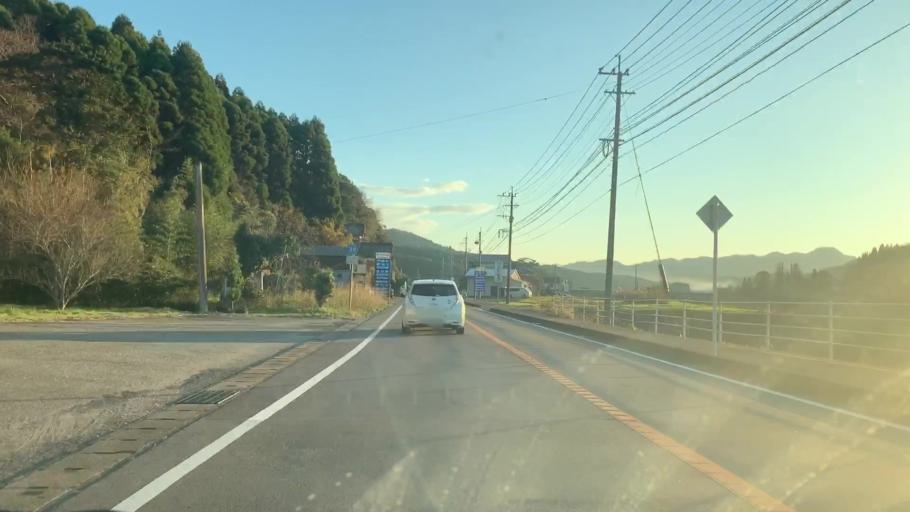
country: JP
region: Saga Prefecture
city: Imaricho-ko
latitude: 33.2703
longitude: 129.9646
